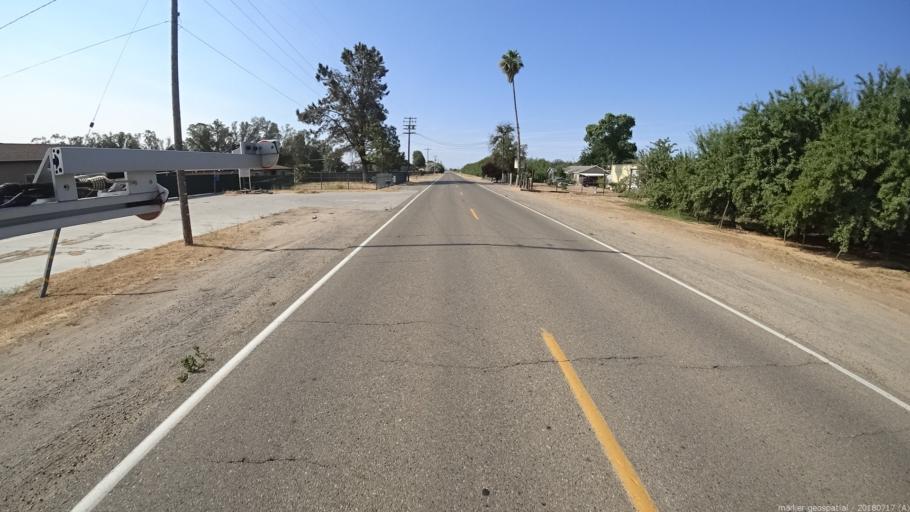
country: US
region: California
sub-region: Madera County
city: Madera Acres
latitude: 37.0322
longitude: -120.1107
